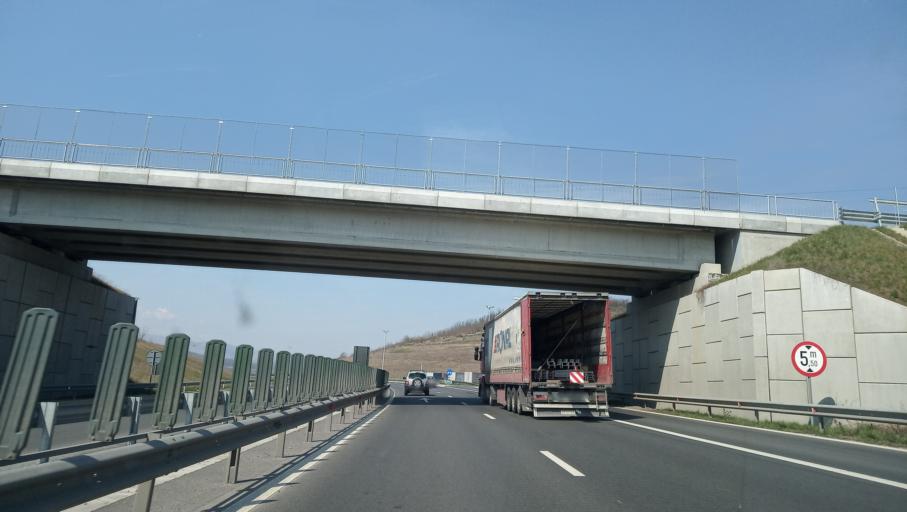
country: RO
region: Alba
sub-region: Comuna Miraslau
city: Miraslau
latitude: 46.3429
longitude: 23.7328
